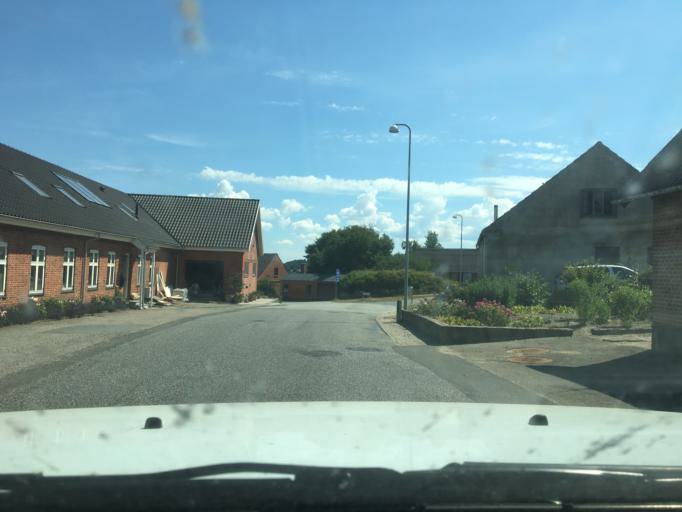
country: DK
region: Central Jutland
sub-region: Randers Kommune
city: Assentoft
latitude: 56.3634
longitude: 10.1482
